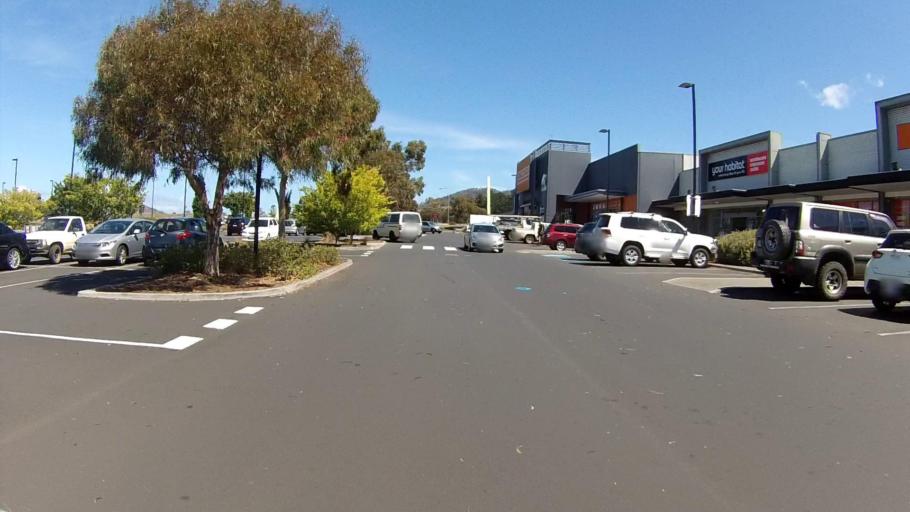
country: AU
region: Tasmania
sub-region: Clarence
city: Cambridge
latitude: -42.8335
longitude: 147.4667
